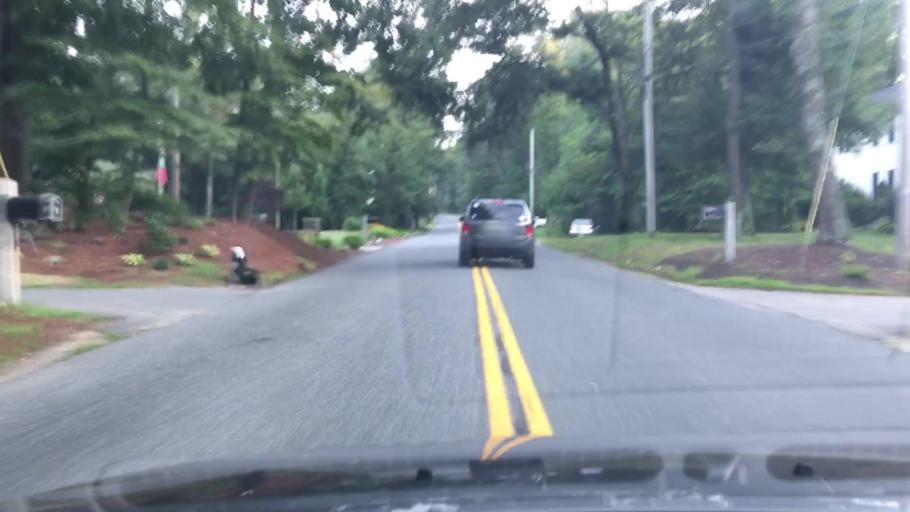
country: US
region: Massachusetts
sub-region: Middlesex County
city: Hopkinton
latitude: 42.1889
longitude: -71.5394
